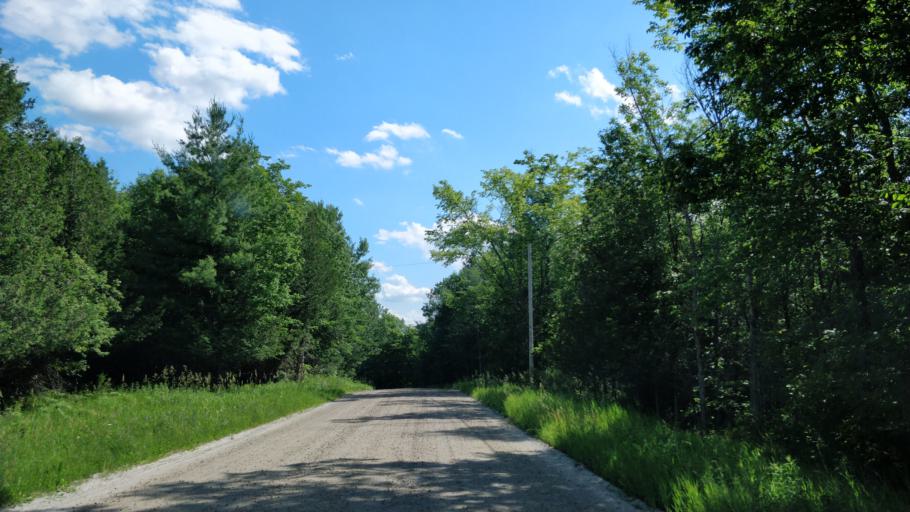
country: CA
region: Ontario
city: Perth
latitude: 44.7318
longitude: -76.5067
